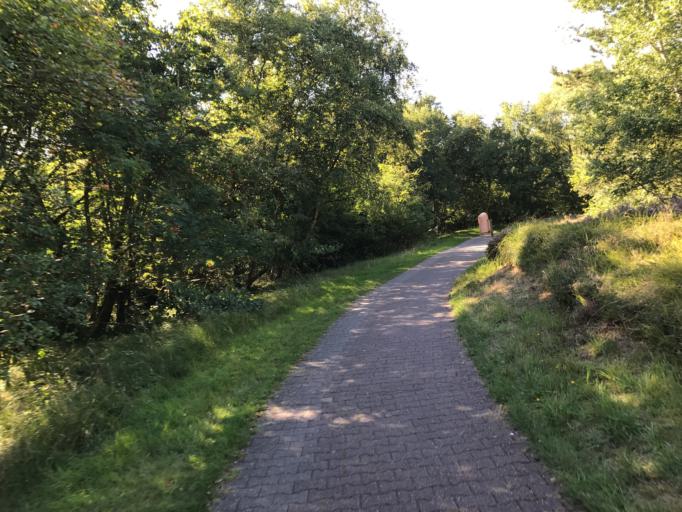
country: DE
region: Lower Saxony
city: Borkum
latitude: 53.5760
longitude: 6.6976
